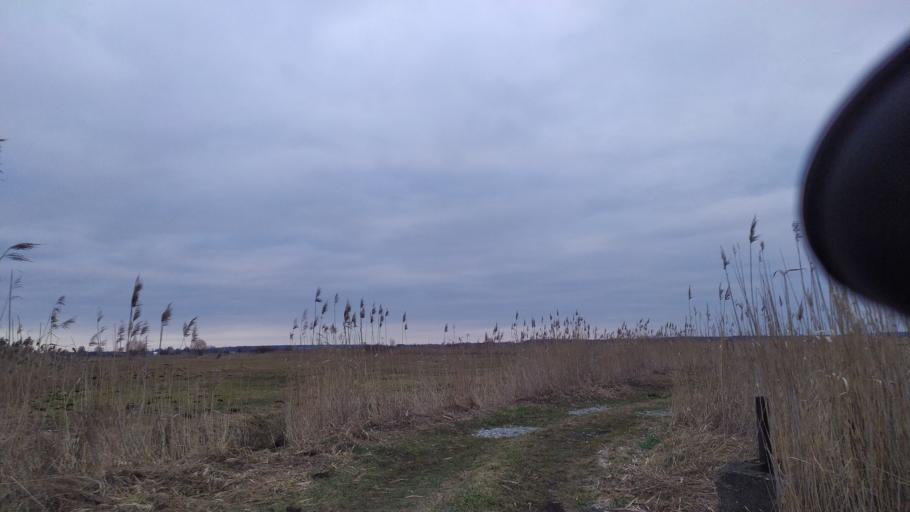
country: PL
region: Lublin Voivodeship
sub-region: Powiat lubartowski
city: Abramow
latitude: 51.4317
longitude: 22.2883
